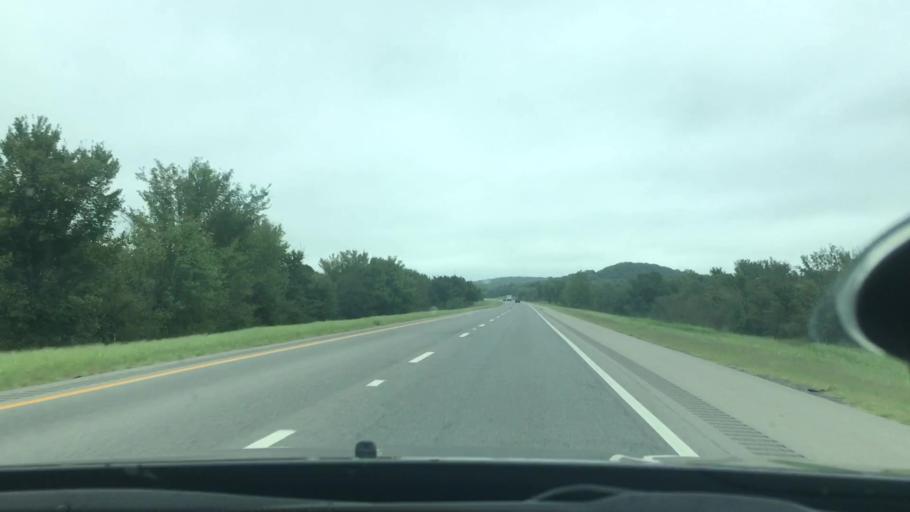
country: US
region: Oklahoma
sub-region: Muskogee County
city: Warner
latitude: 35.4564
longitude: -95.4096
